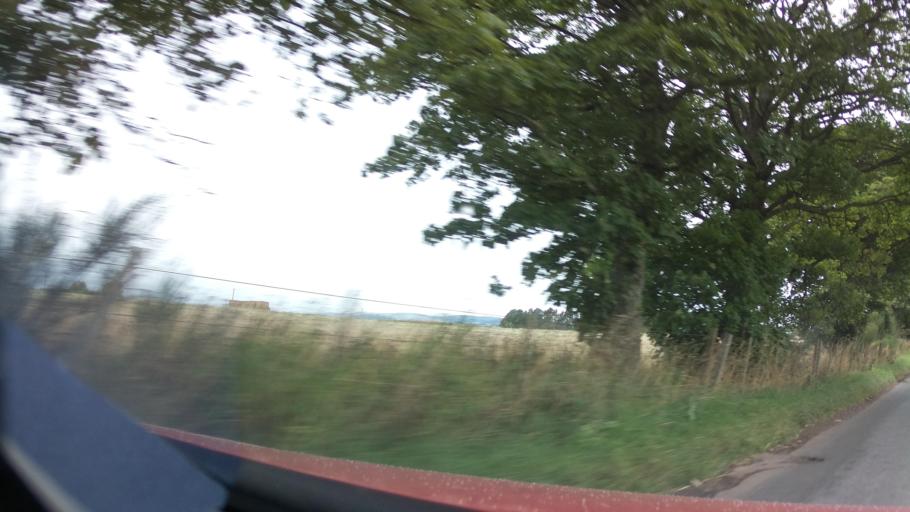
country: GB
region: Scotland
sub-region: Perth and Kinross
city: Milnathort
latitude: 56.2311
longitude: -3.3609
